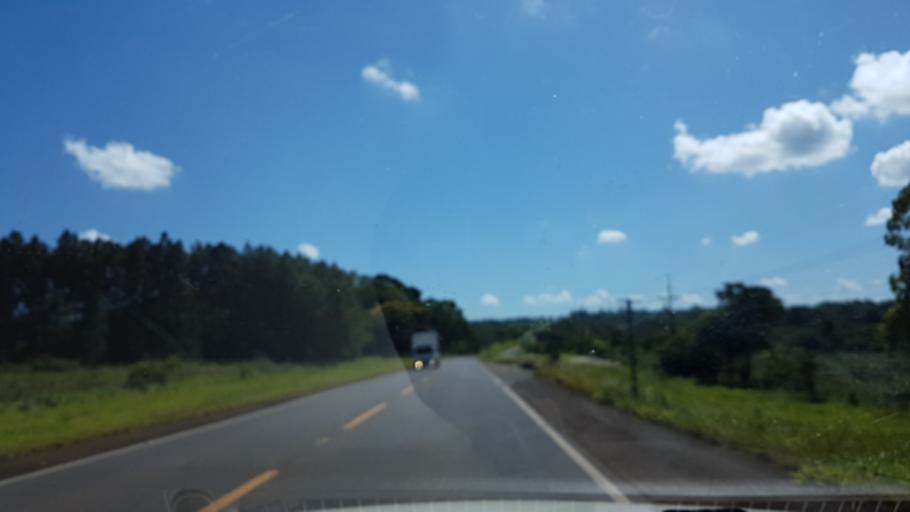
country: PY
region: Itapua
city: Carmen del Parana
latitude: -27.2121
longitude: -56.0856
